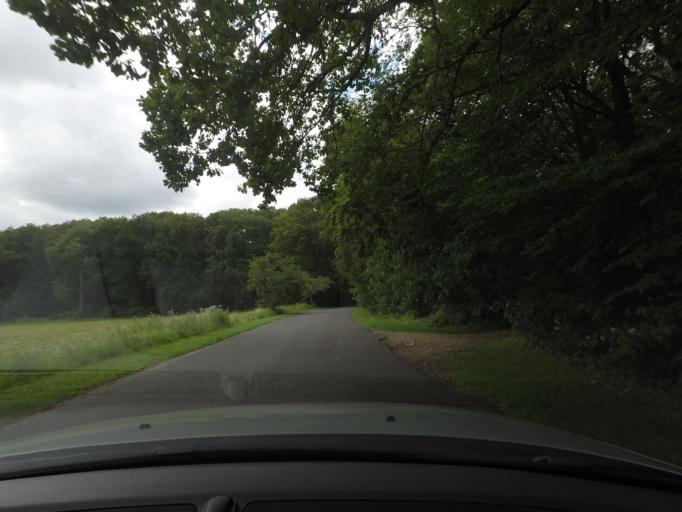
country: FR
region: Haute-Normandie
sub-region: Departement de l'Eure
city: Les Andelys
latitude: 49.2375
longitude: 1.4117
